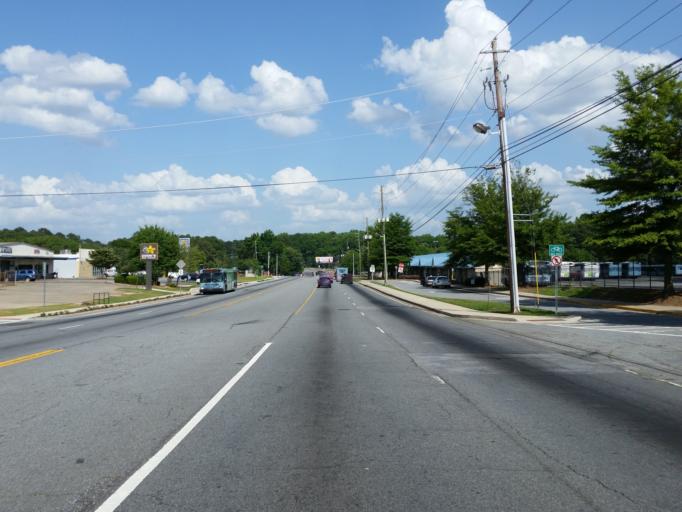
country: US
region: Georgia
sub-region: Cobb County
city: Marietta
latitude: 33.9424
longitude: -84.5313
